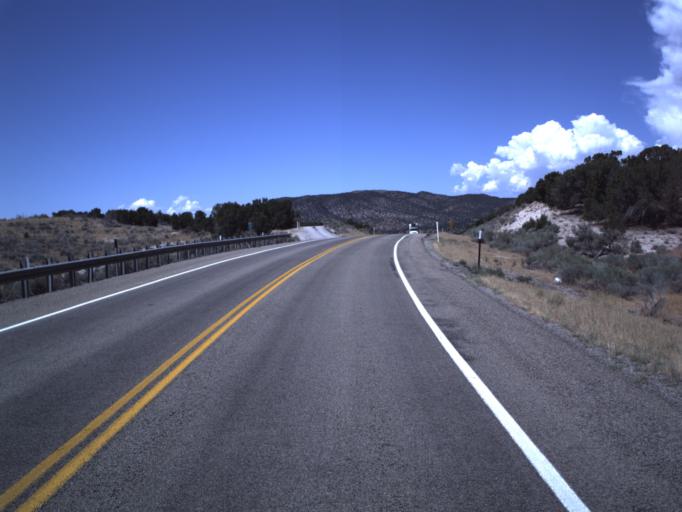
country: US
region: Utah
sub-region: Juab County
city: Nephi
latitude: 39.6658
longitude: -112.0474
